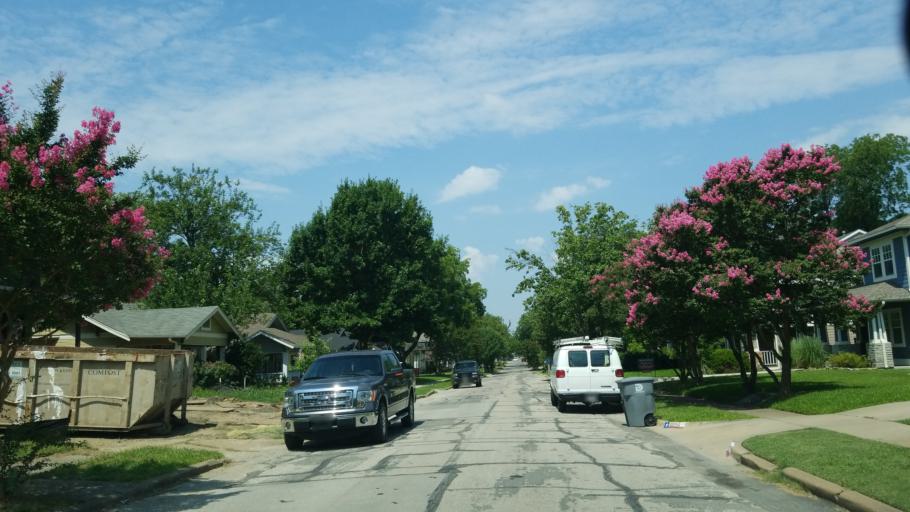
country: US
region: Texas
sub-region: Dallas County
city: Highland Park
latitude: 32.8203
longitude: -96.7725
